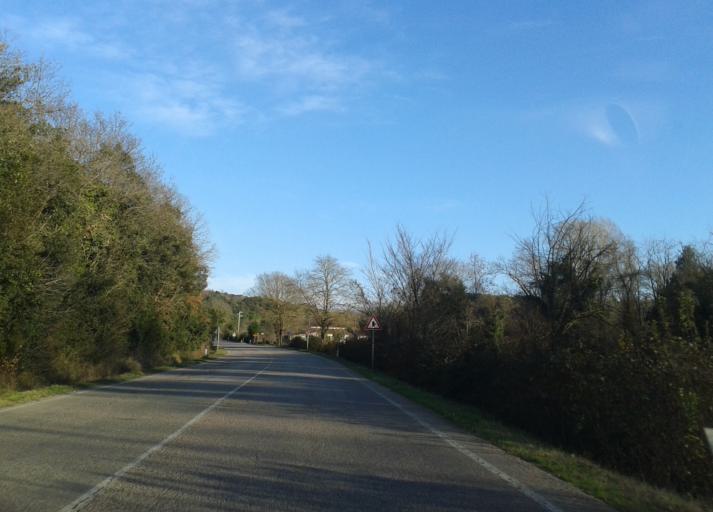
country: IT
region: Tuscany
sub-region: Provincia di Livorno
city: Guasticce
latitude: 43.5655
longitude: 10.3889
